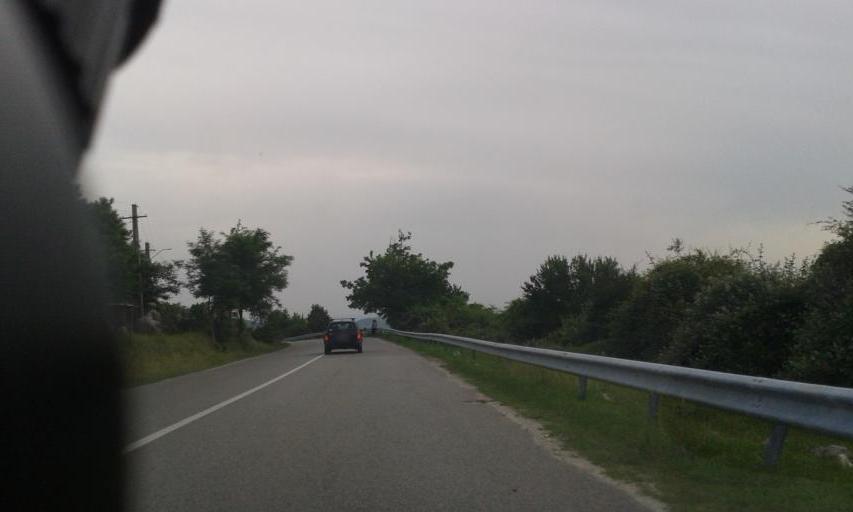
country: RO
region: Gorj
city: Novaci-Straini
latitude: 45.1887
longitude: 23.6824
